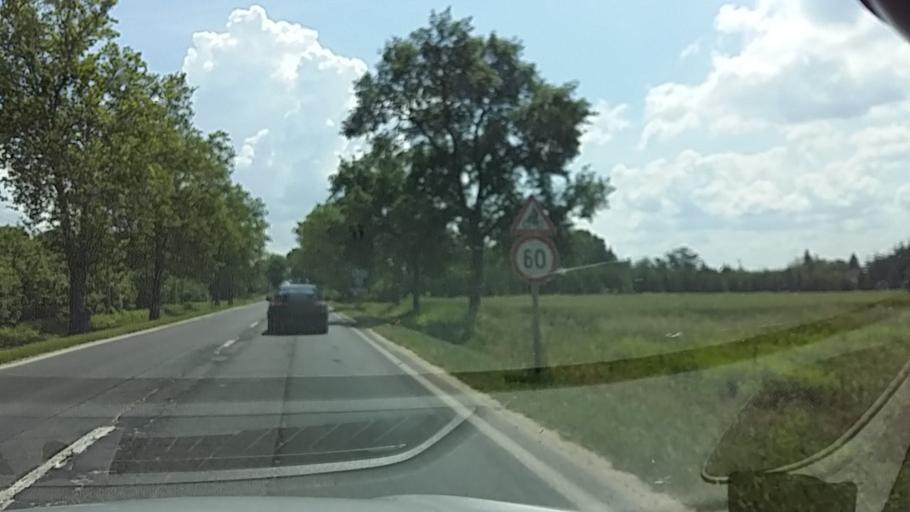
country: AT
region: Burgenland
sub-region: Politischer Bezirk Gussing
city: Heiligenbrunn
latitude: 46.9685
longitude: 16.4225
